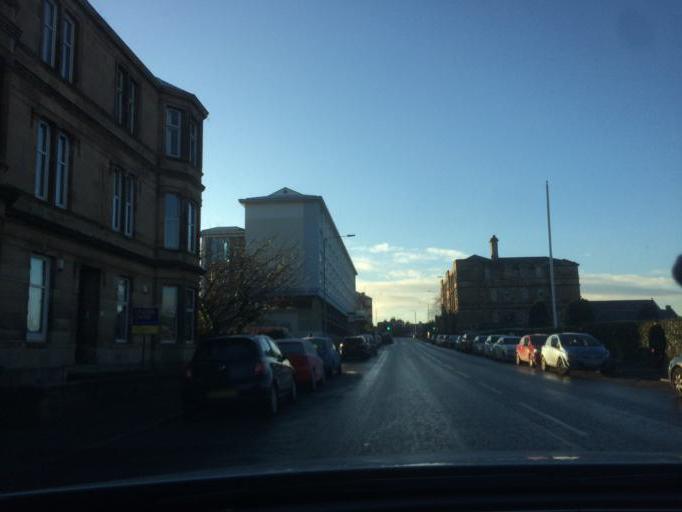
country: GB
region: Scotland
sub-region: East Renfrewshire
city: Giffnock
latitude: 55.8299
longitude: -4.2830
